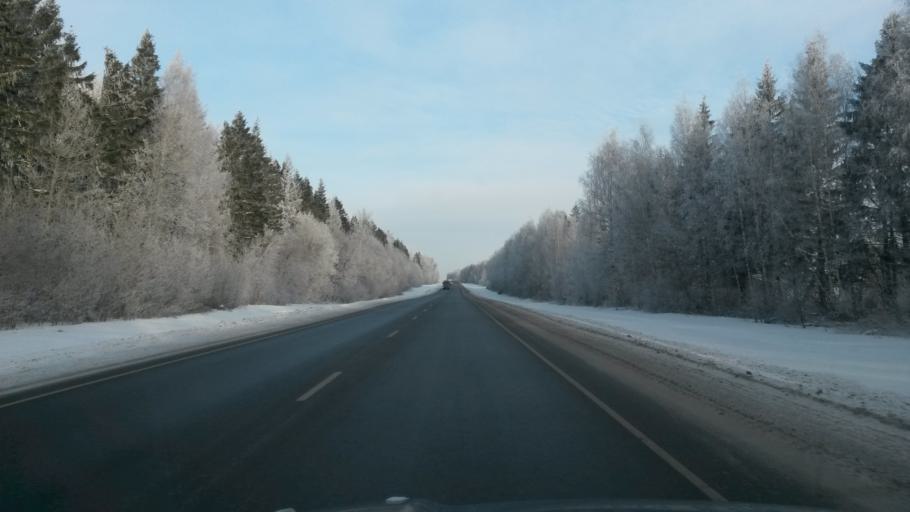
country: RU
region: Vladimir
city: Bogolyubovo
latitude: 56.2293
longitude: 40.4456
